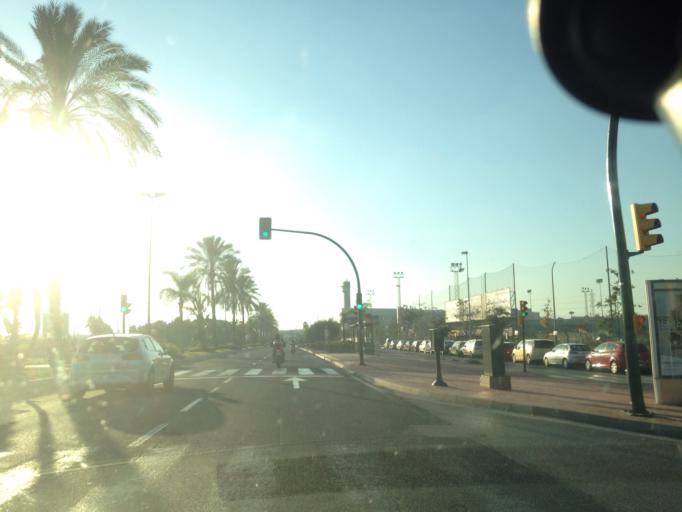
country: ES
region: Andalusia
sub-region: Provincia de Malaga
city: Malaga
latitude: 36.7074
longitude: -4.4612
